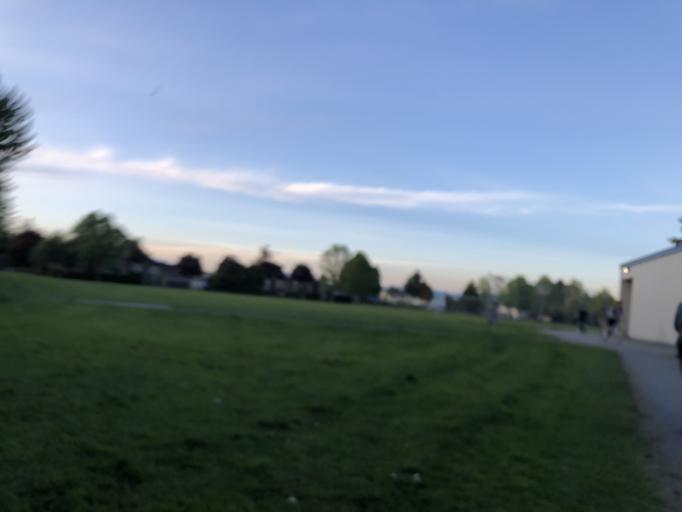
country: CA
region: British Columbia
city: Richmond
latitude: 49.1449
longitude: -123.1216
